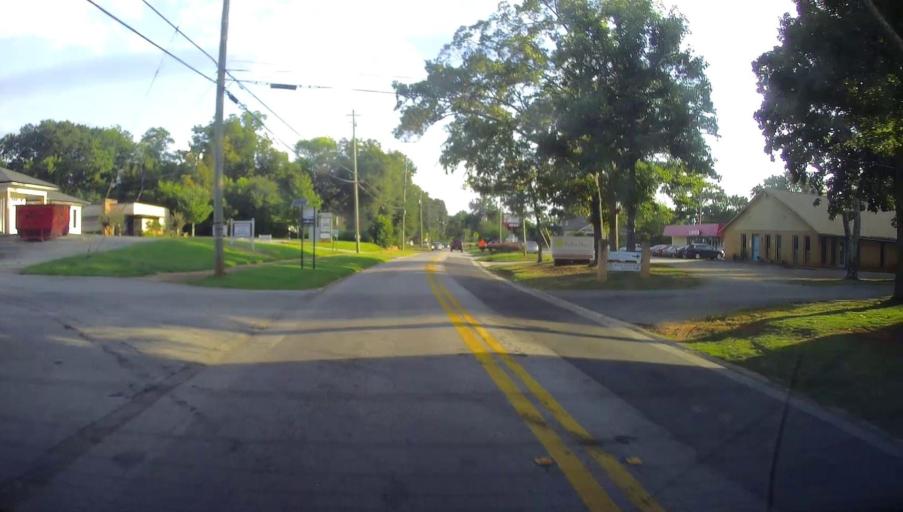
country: US
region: Georgia
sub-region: Monroe County
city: Forsyth
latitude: 33.0310
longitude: -83.9465
